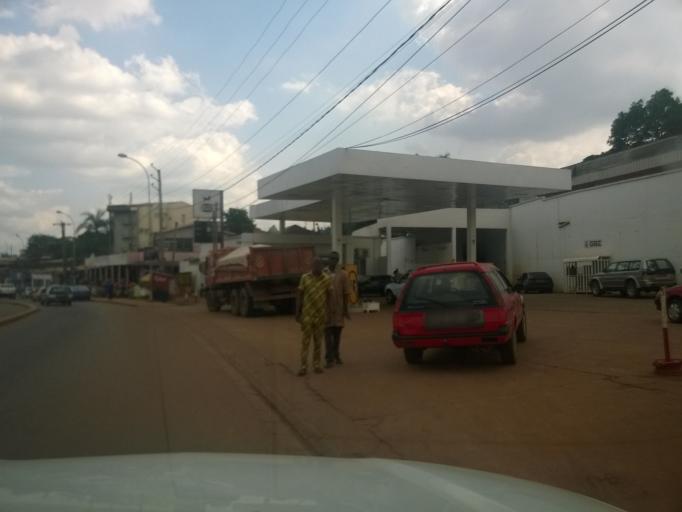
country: CM
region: Centre
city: Yaounde
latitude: 3.8500
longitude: 11.5151
